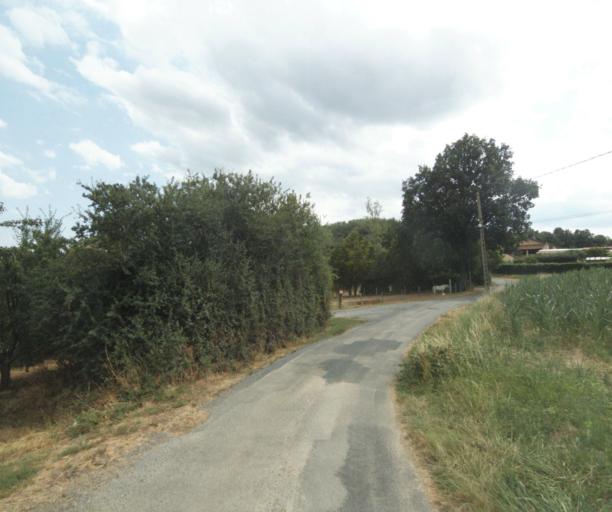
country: FR
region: Rhone-Alpes
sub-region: Departement du Rhone
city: Bully
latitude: 45.8825
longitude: 4.5699
